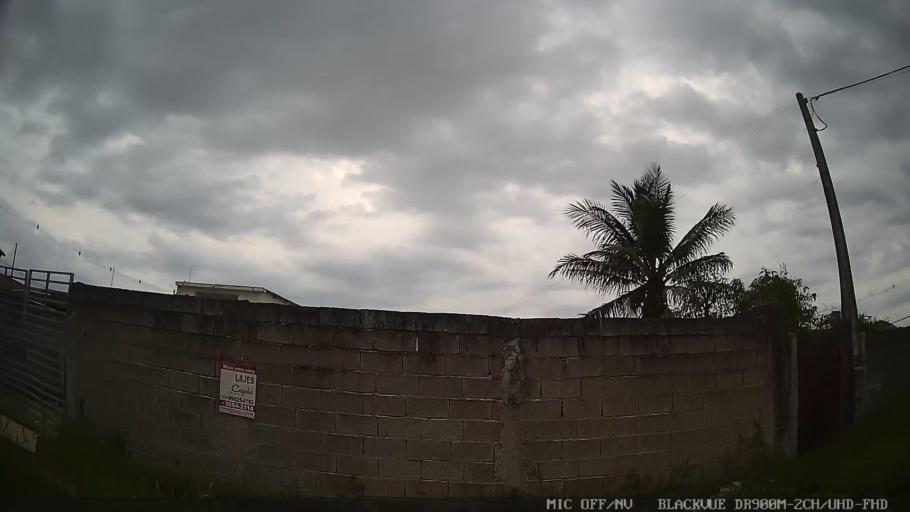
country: BR
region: Sao Paulo
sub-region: Caraguatatuba
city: Caraguatatuba
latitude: -23.6852
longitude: -45.4550
